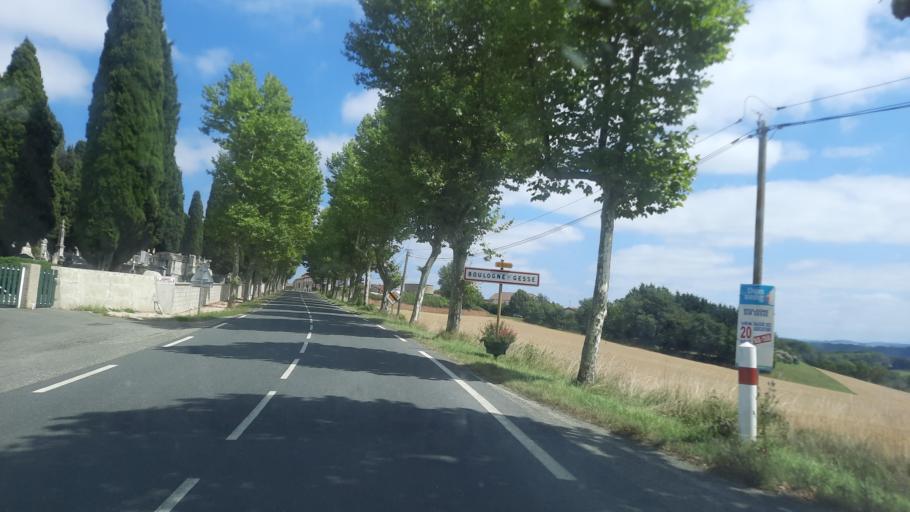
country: FR
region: Midi-Pyrenees
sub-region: Departement de la Haute-Garonne
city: Boulogne-sur-Gesse
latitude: 43.2890
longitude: 0.6393
